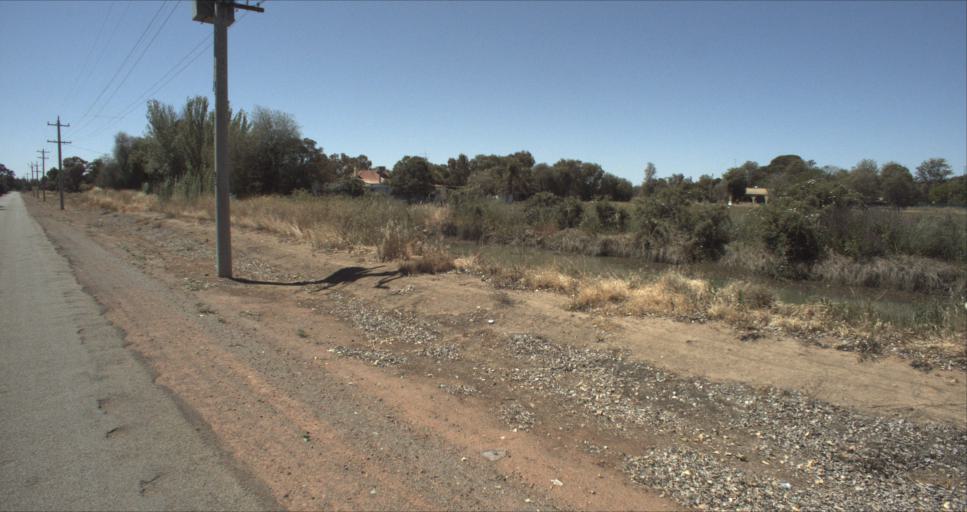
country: AU
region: New South Wales
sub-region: Leeton
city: Leeton
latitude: -34.5281
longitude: 146.3296
